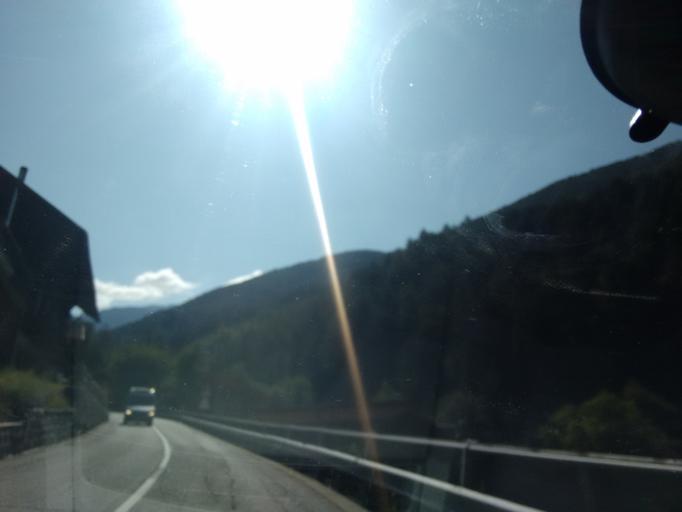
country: IT
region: Trentino-Alto Adige
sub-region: Bolzano
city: Velturno
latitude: 46.6470
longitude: 11.6144
